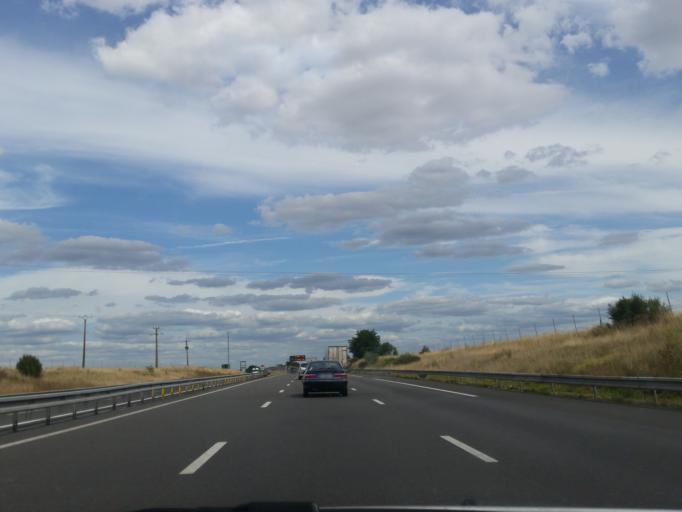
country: FR
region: Centre
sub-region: Departement du Loir-et-Cher
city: Saint-Sulpice-de-Pommeray
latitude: 47.6161
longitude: 1.2916
